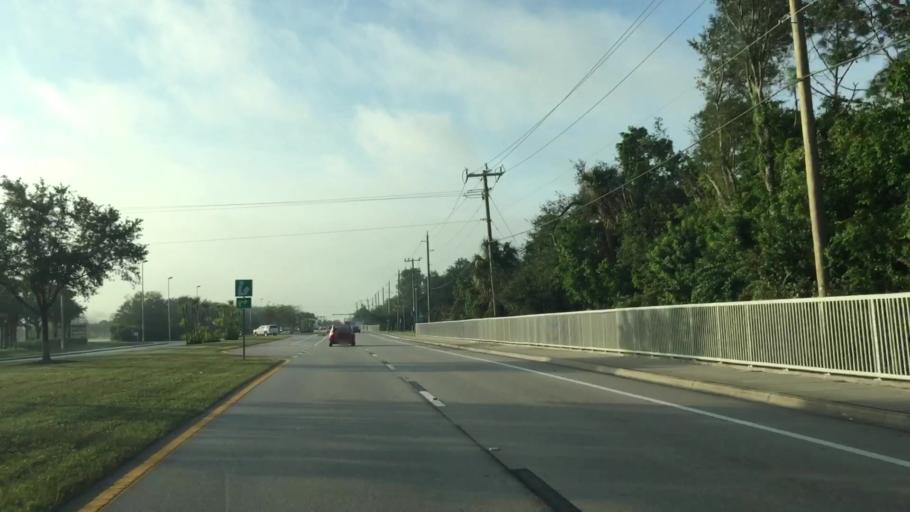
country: US
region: Florida
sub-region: Lee County
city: Estero
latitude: 26.4354
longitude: -81.7887
